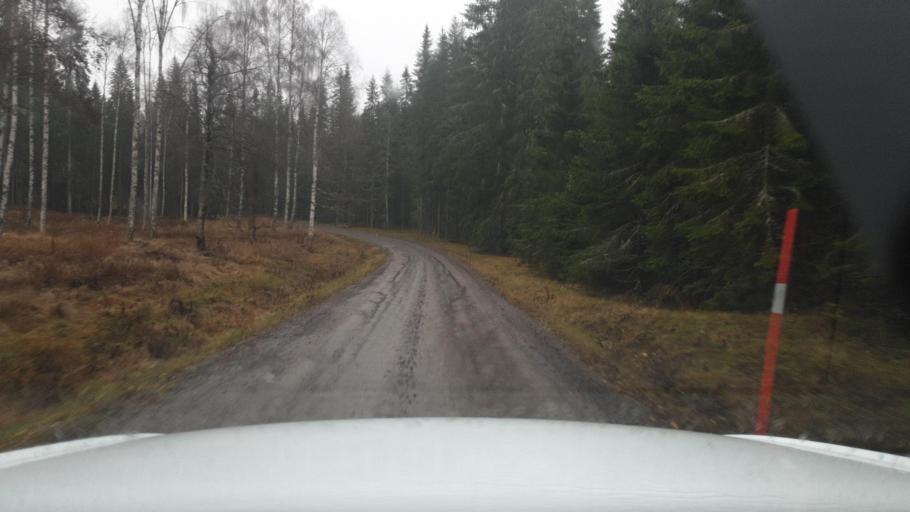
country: SE
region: Vaermland
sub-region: Sunne Kommun
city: Sunne
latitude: 59.8584
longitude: 12.8850
